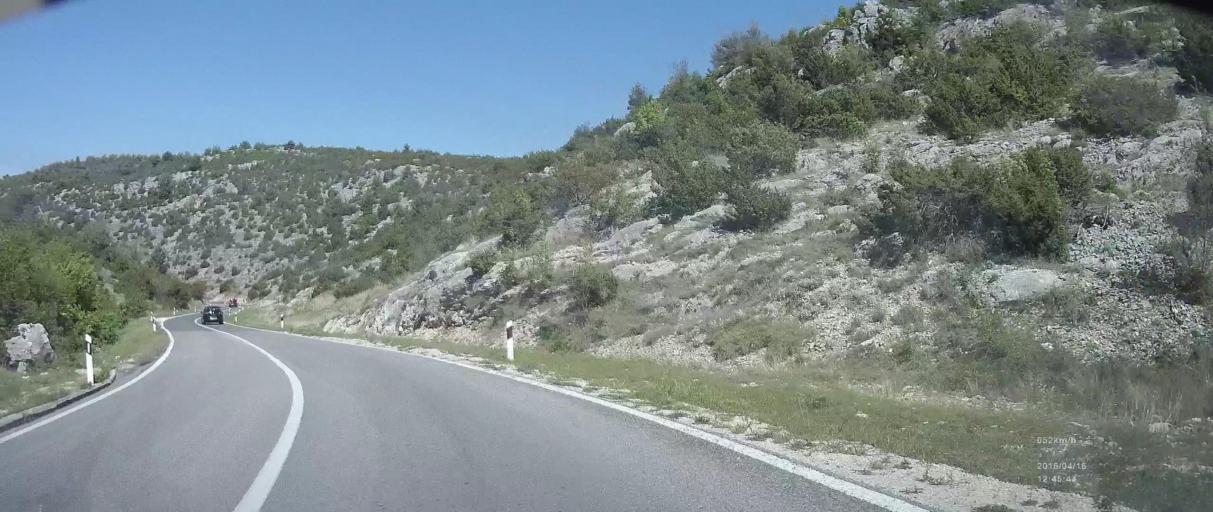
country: HR
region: Sibensko-Kniniska
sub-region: Grad Sibenik
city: Brodarica
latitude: 43.6505
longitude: 16.0601
